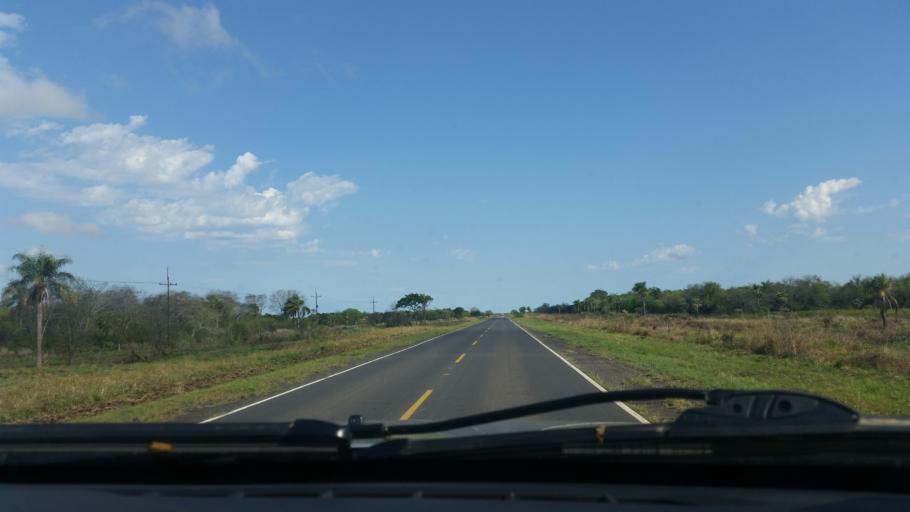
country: PY
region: Presidente Hayes
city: Benjamin Aceval
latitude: -24.9029
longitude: -57.6524
